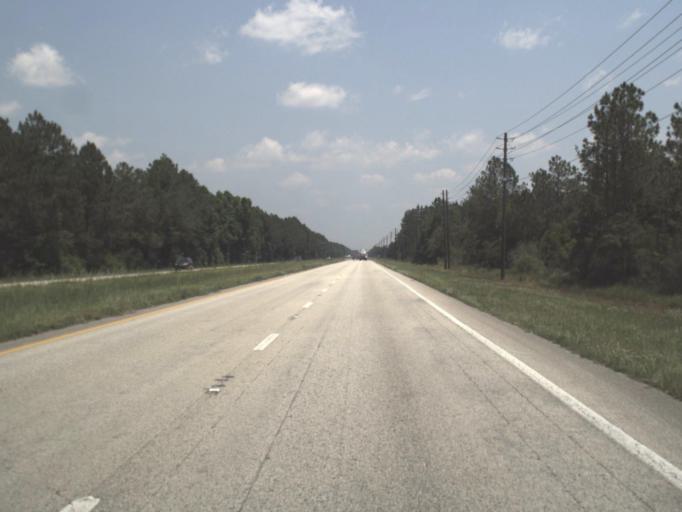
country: US
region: Florida
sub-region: Duval County
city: Baldwin
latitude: 30.2311
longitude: -82.0032
